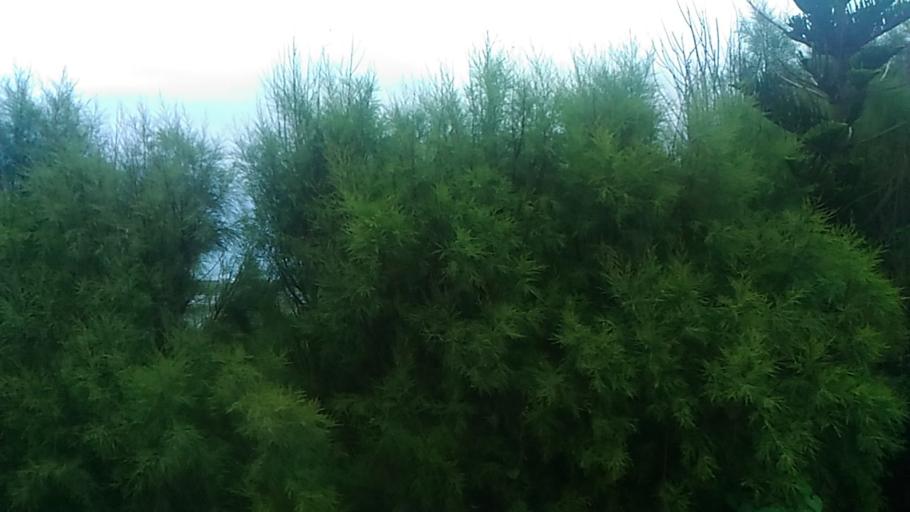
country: TW
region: Taiwan
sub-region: Penghu
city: Ma-kung
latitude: 23.3661
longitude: 119.5082
